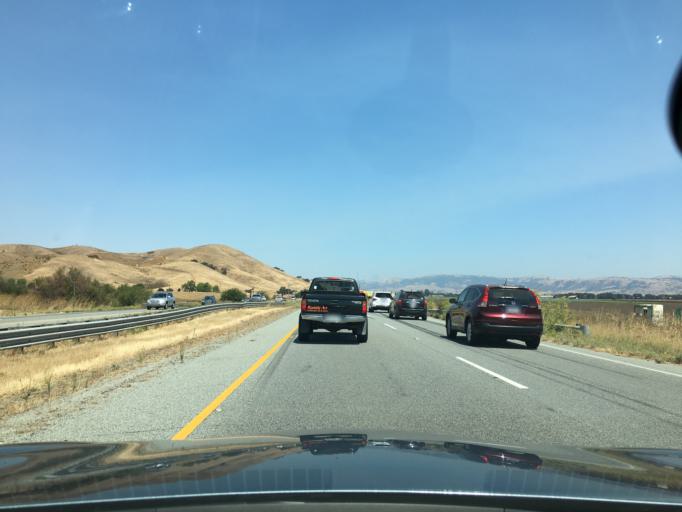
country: US
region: California
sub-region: Santa Clara County
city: Gilroy
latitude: 36.9423
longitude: -121.5525
